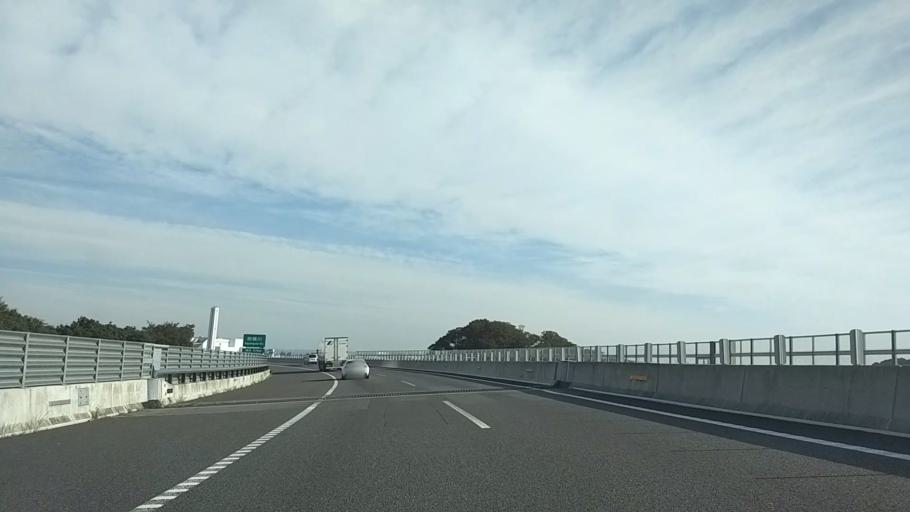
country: JP
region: Kanagawa
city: Atsugi
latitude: 35.4511
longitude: 139.3743
